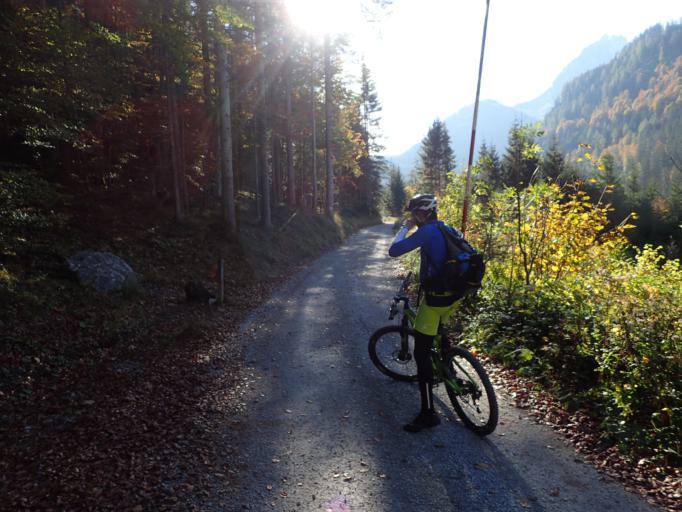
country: AT
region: Salzburg
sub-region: Politischer Bezirk Sankt Johann im Pongau
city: Pfarrwerfen
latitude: 47.4389
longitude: 13.1865
